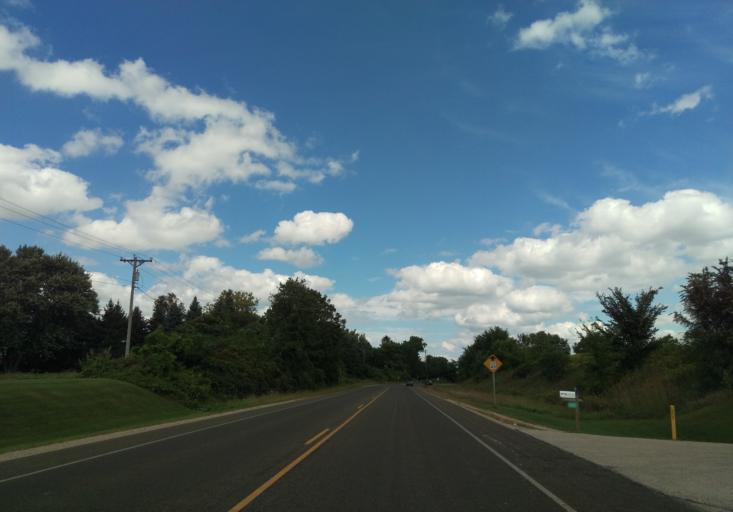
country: US
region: Wisconsin
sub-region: Dane County
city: Waunakee
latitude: 43.1421
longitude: -89.4422
